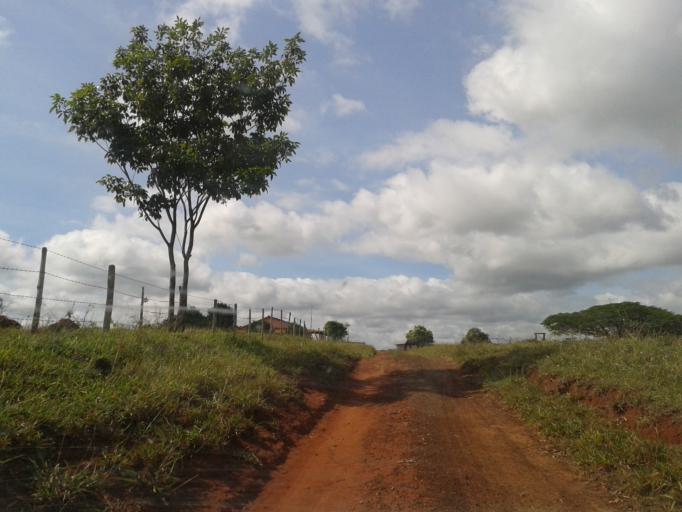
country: BR
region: Minas Gerais
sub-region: Campina Verde
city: Campina Verde
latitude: -19.4290
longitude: -49.6654
